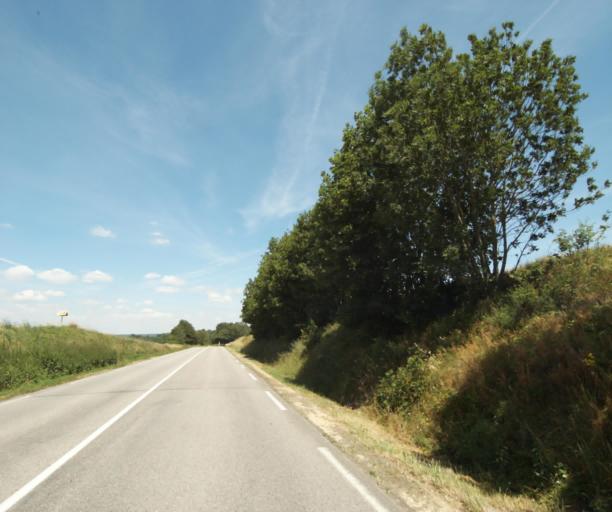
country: FR
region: Lorraine
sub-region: Departement de Meurthe-et-Moselle
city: Luneville
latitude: 48.6191
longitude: 6.4870
